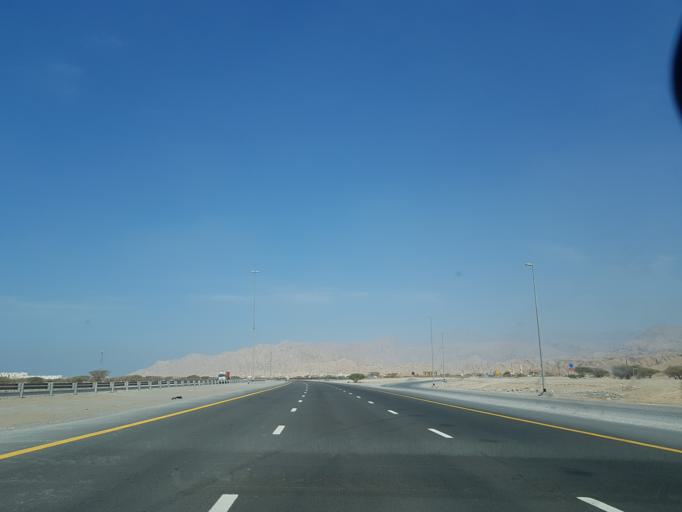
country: AE
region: Ra's al Khaymah
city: Ras al-Khaimah
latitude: 25.7790
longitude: 56.0306
